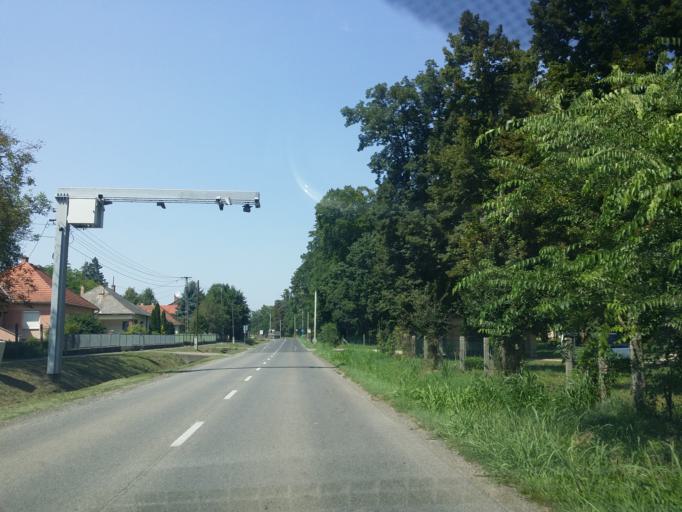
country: HU
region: Tolna
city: Hogyesz
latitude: 46.4985
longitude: 18.4162
